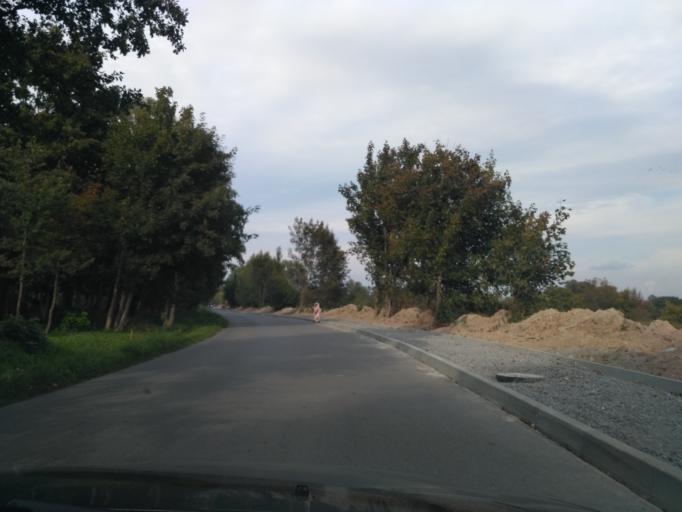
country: PL
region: Subcarpathian Voivodeship
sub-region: Powiat rzeszowski
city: Swilcza
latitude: 50.0866
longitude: 21.9152
